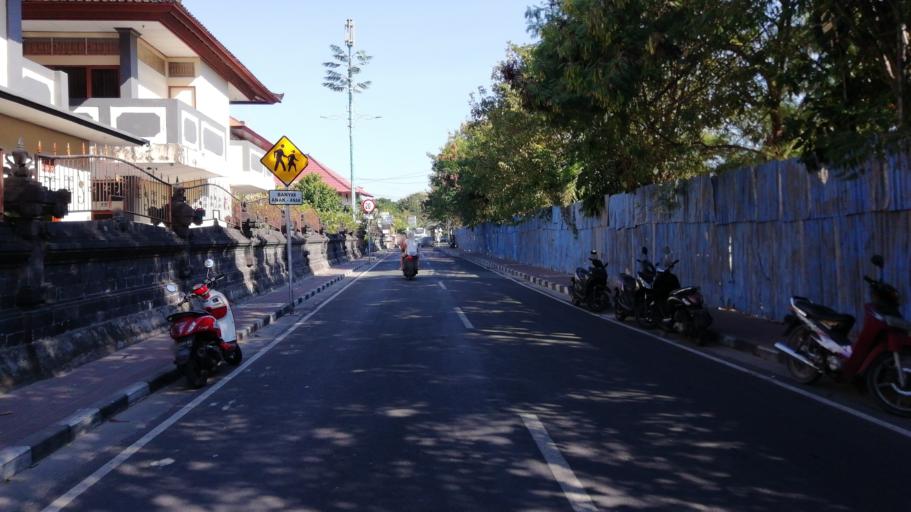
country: ID
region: Bali
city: Bualu
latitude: -8.7609
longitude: 115.2219
